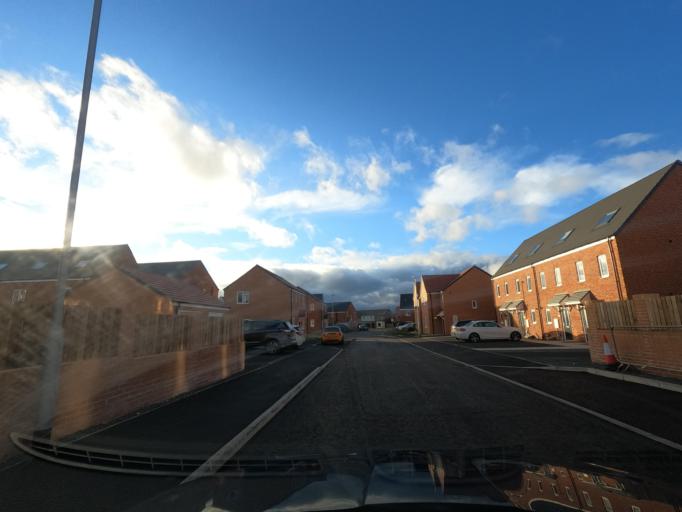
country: GB
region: England
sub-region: Northumberland
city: Cramlington
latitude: 55.0891
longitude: -1.5929
